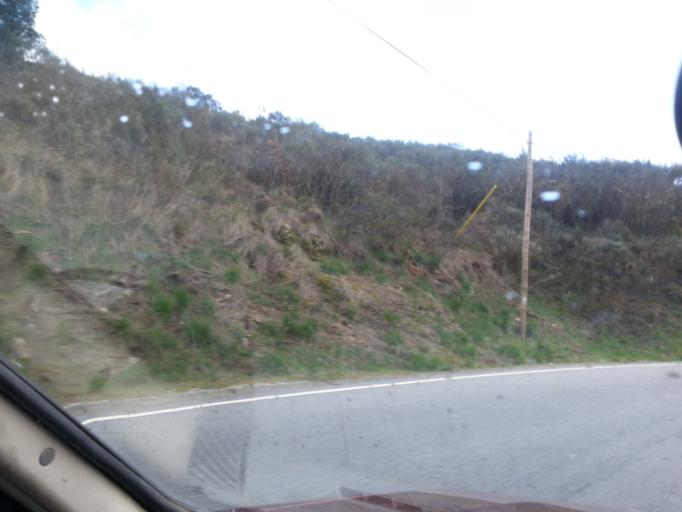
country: PT
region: Guarda
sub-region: Guarda
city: Guarda
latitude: 40.5461
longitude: -7.3232
